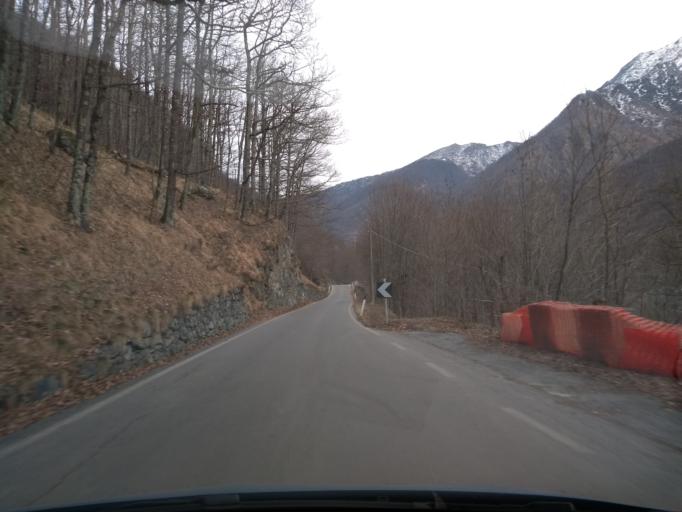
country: IT
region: Piedmont
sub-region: Provincia di Torino
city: Lemie
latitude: 45.2279
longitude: 7.2990
